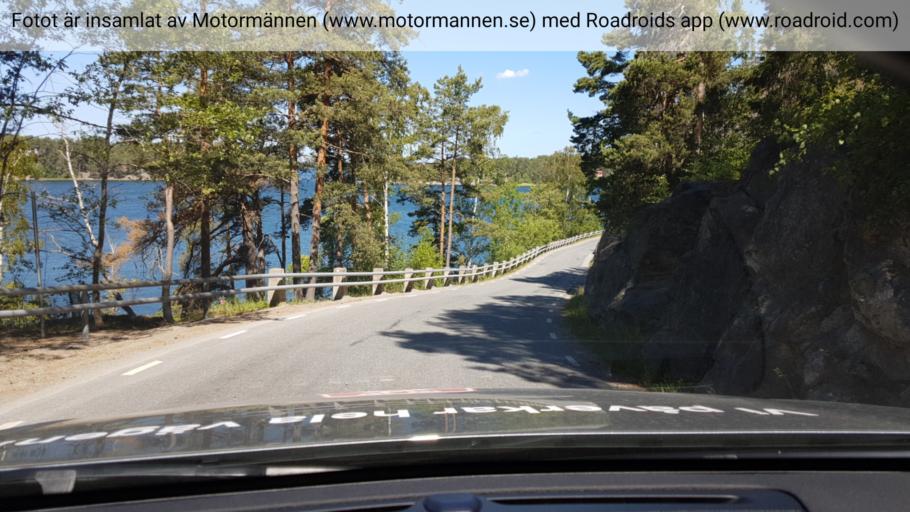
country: SE
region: Stockholm
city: Dalaro
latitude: 59.1504
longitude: 18.4333
